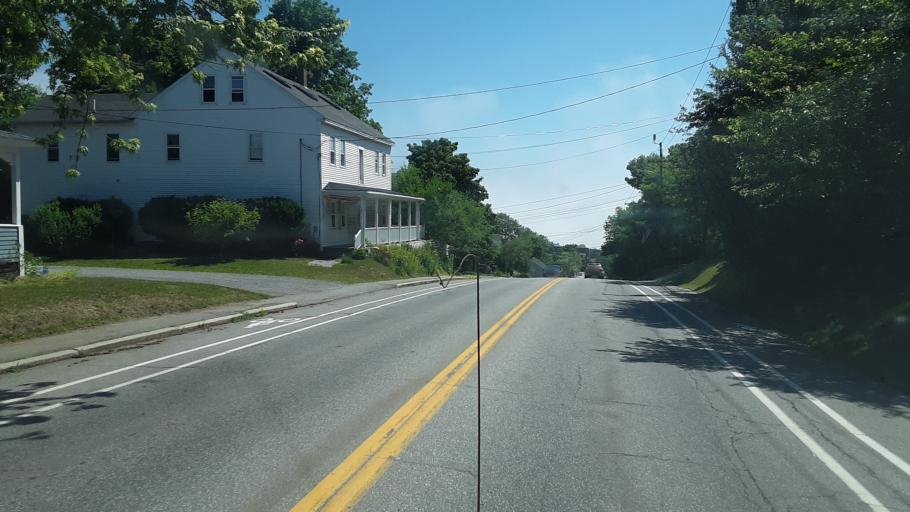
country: US
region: Maine
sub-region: Waldo County
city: Belfast
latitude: 44.4248
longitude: -69.0131
